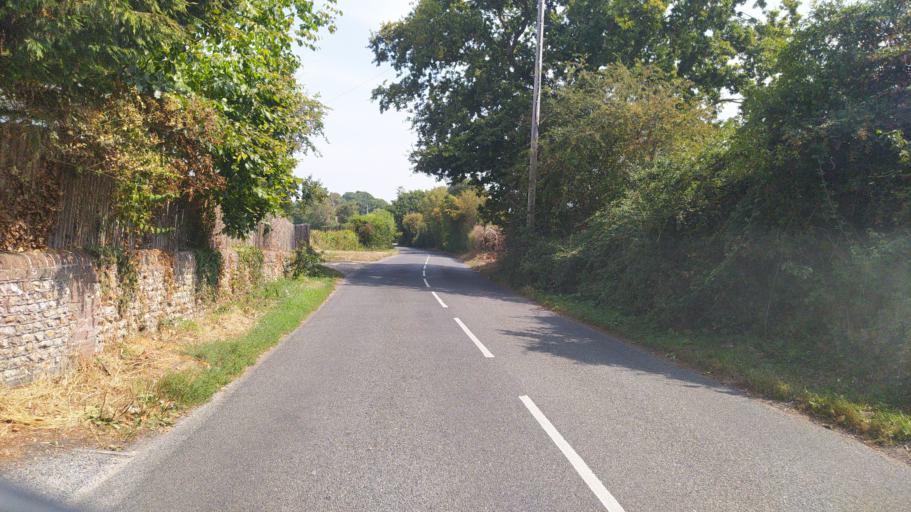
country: GB
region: England
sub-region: Hampshire
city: Emsworth
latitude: 50.8618
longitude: -0.9576
